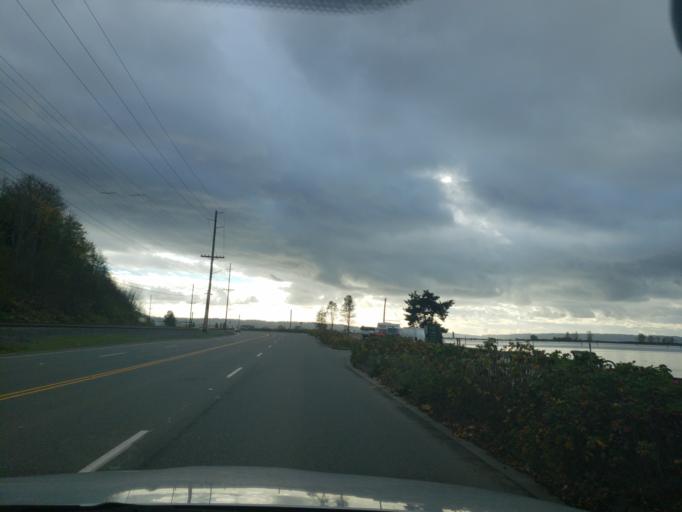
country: US
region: Washington
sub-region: Snohomish County
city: Everett
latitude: 48.0108
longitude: -122.2124
